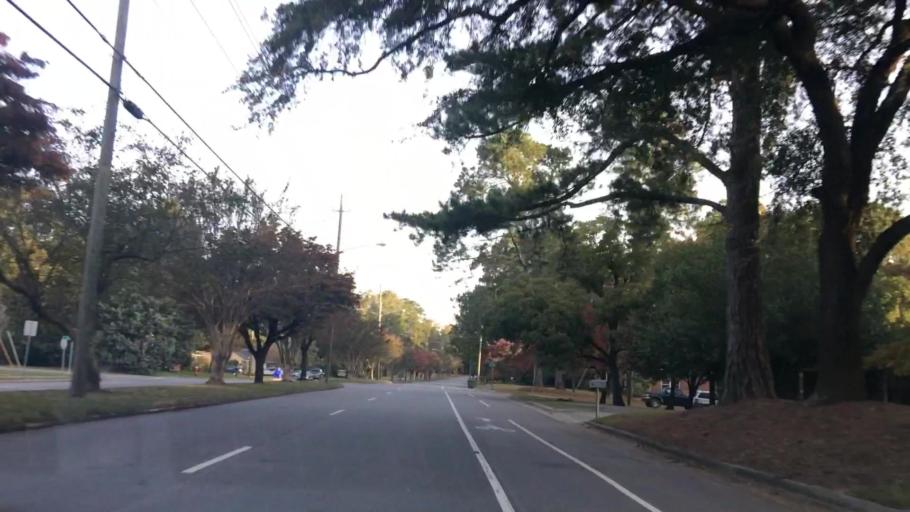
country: US
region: North Carolina
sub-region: Pitt County
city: Greenville
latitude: 35.5914
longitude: -77.3607
